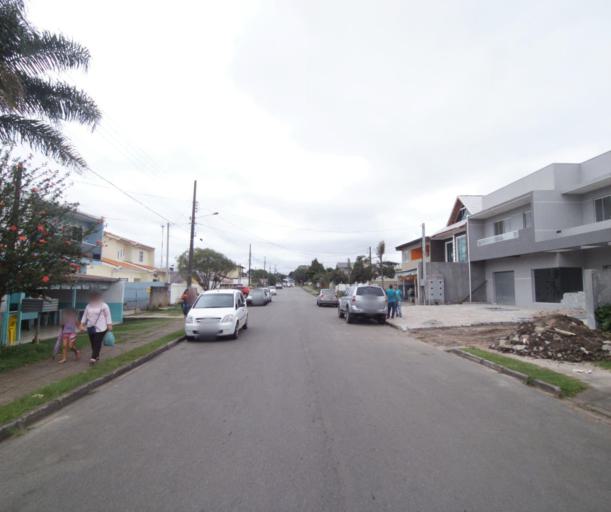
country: BR
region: Parana
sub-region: Quatro Barras
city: Quatro Barras
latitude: -25.3626
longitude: -49.1028
